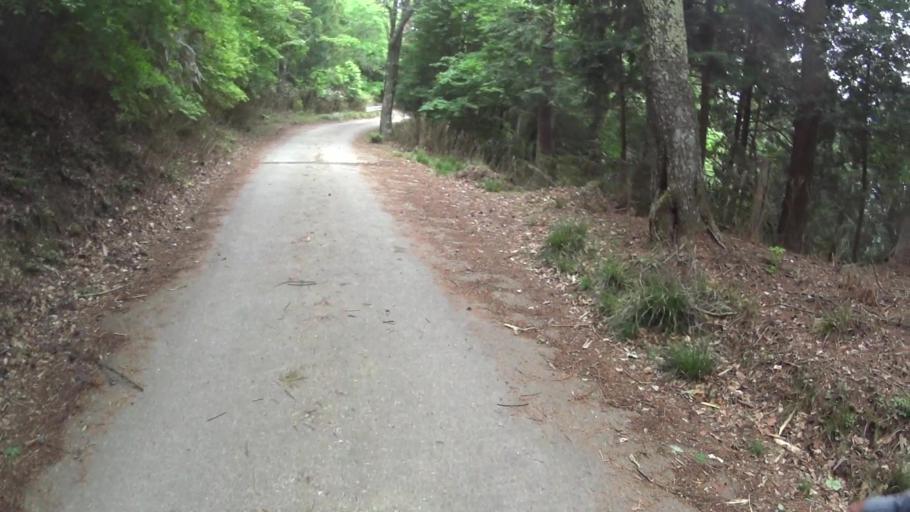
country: JP
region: Nara
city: Yoshino-cho
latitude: 34.3475
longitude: 135.8789
